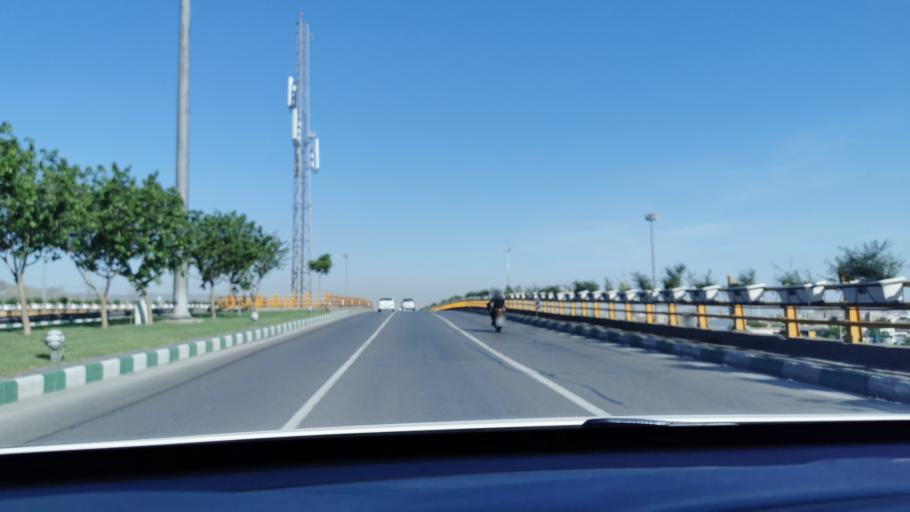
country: IR
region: Razavi Khorasan
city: Mashhad
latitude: 36.2554
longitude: 59.6005
